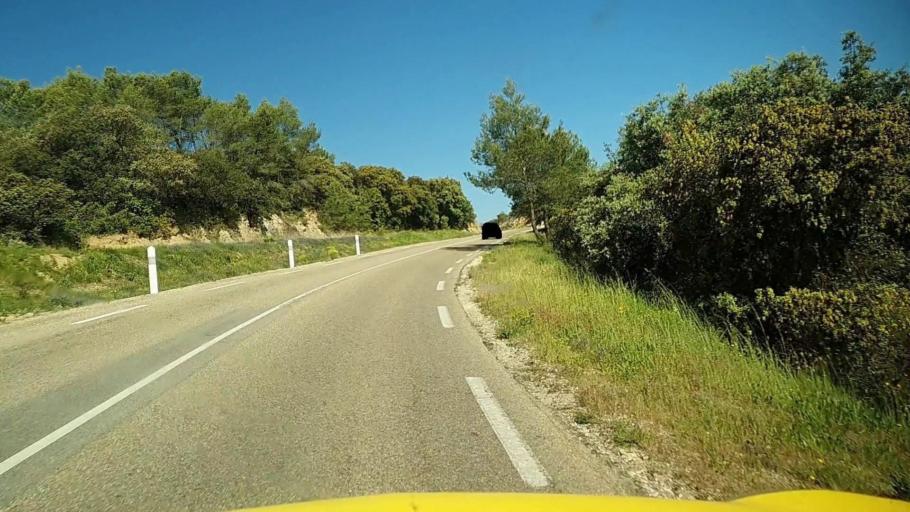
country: FR
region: Languedoc-Roussillon
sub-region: Departement du Gard
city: Poulx
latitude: 43.9141
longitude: 4.3950
